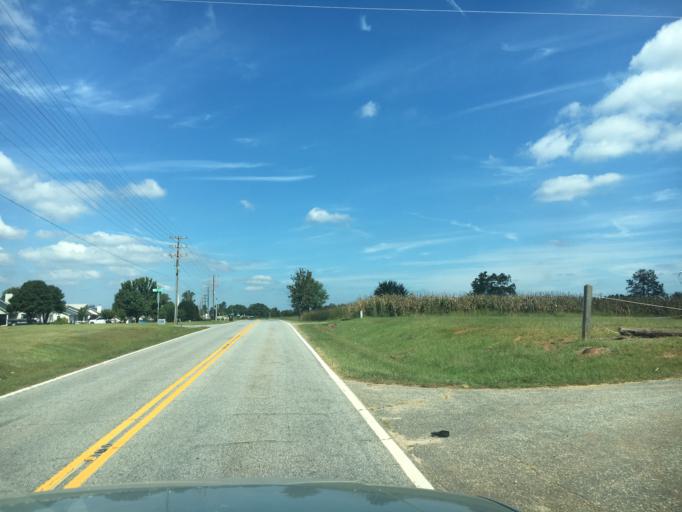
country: US
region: South Carolina
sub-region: Spartanburg County
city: Boiling Springs
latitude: 35.0797
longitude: -81.9286
